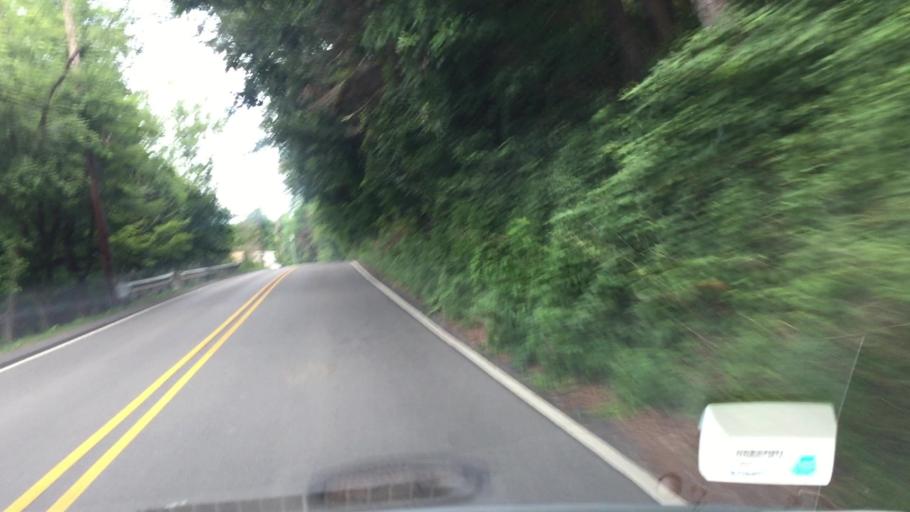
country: US
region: Pennsylvania
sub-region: Allegheny County
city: Franklin Park
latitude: 40.5920
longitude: -80.0372
